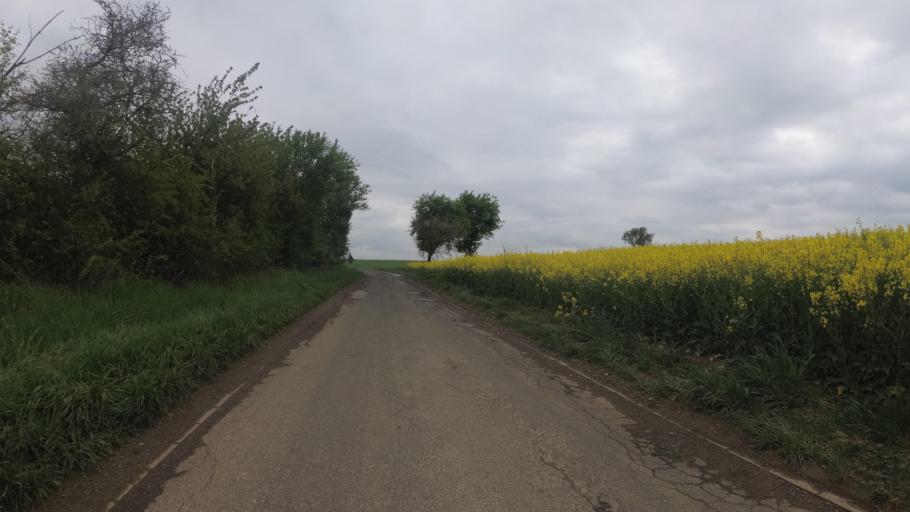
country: DE
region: Saarland
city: Rehlingen-Siersburg
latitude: 49.3748
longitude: 6.6166
